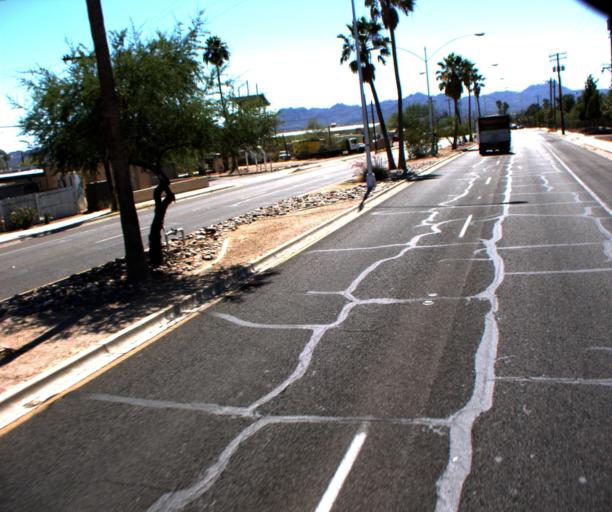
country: US
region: Arizona
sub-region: Pima County
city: Flowing Wells
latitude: 32.2612
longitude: -110.9891
